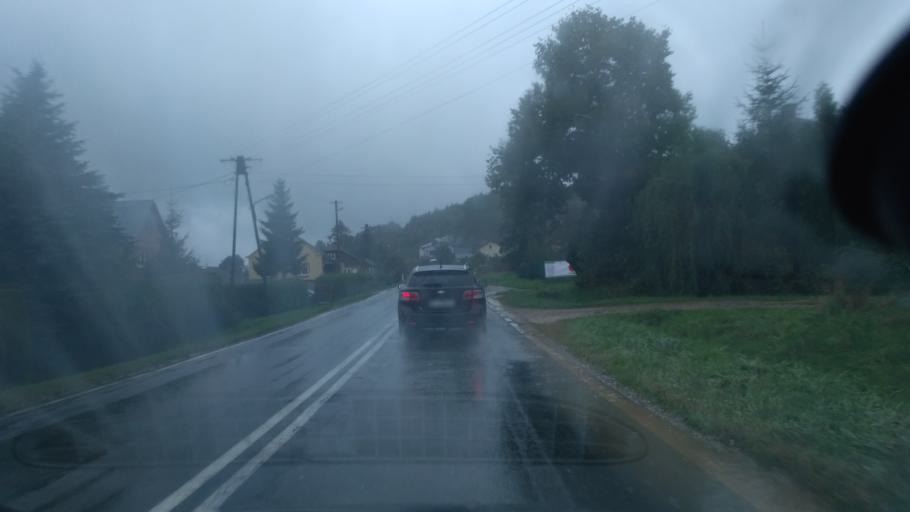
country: PL
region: Subcarpathian Voivodeship
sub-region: Powiat ropczycko-sedziszowski
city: Niedzwiada
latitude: 50.0075
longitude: 21.5540
